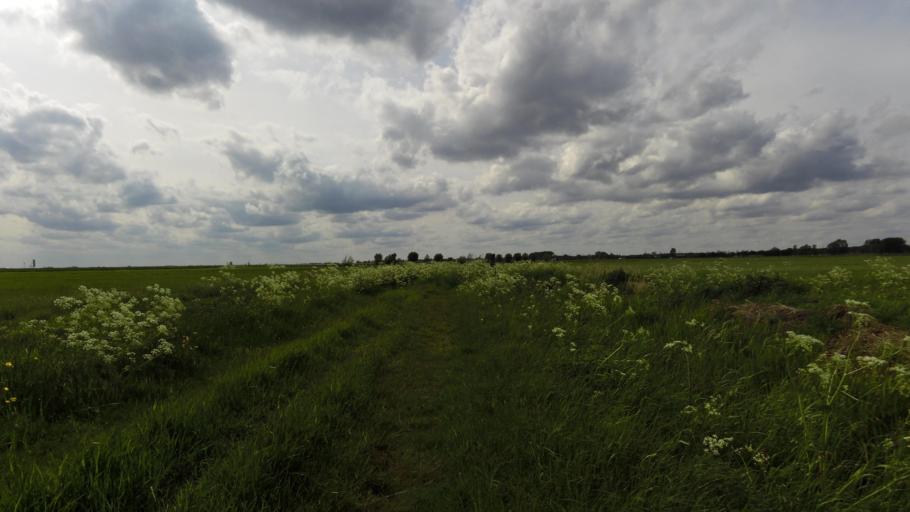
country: NL
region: Gelderland
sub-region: Gemeente Nijkerk
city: Nijkerk
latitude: 52.2496
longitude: 5.4805
